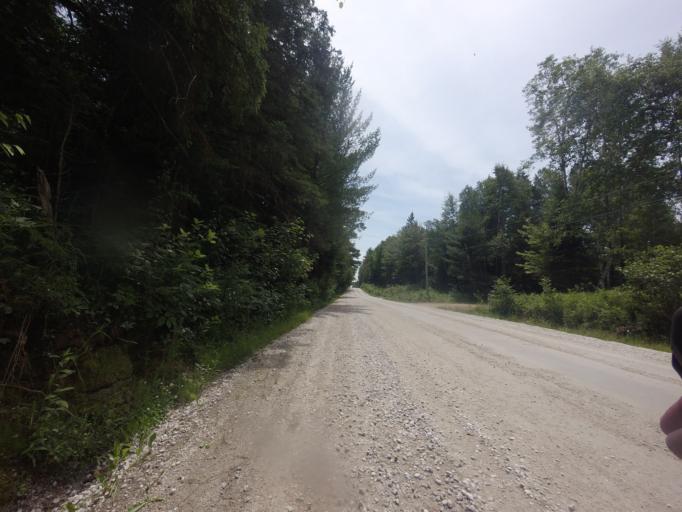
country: CA
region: Quebec
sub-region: Outaouais
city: Wakefield
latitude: 45.9612
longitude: -76.0606
